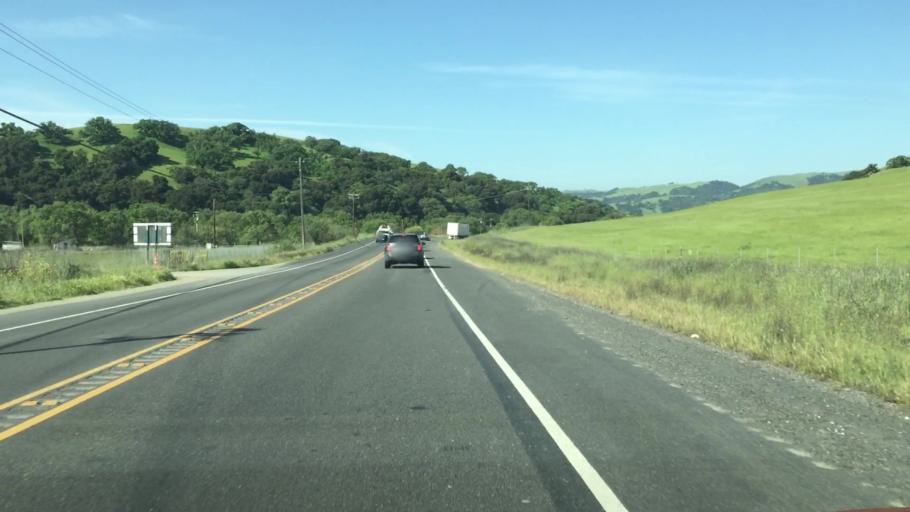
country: US
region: California
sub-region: Alameda County
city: Pleasanton
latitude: 37.5991
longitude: -121.8511
